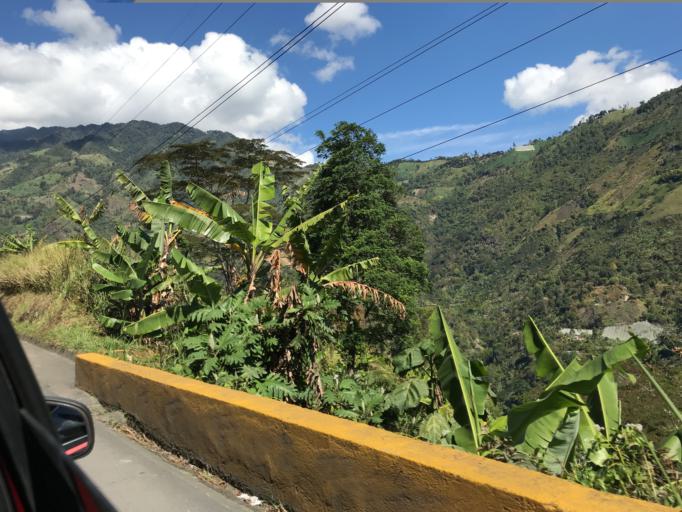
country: CO
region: Tolima
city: Cajamarca
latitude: 4.4404
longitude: -75.4036
